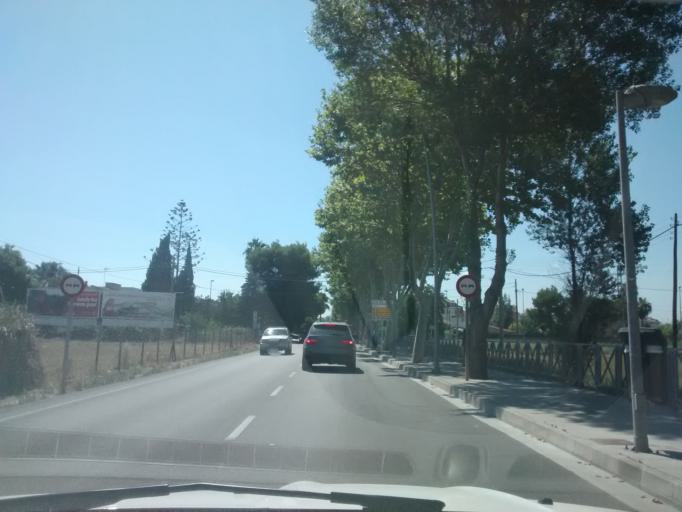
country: ES
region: Balearic Islands
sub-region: Illes Balears
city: Port d'Alcudia
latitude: 39.8470
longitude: 3.1301
